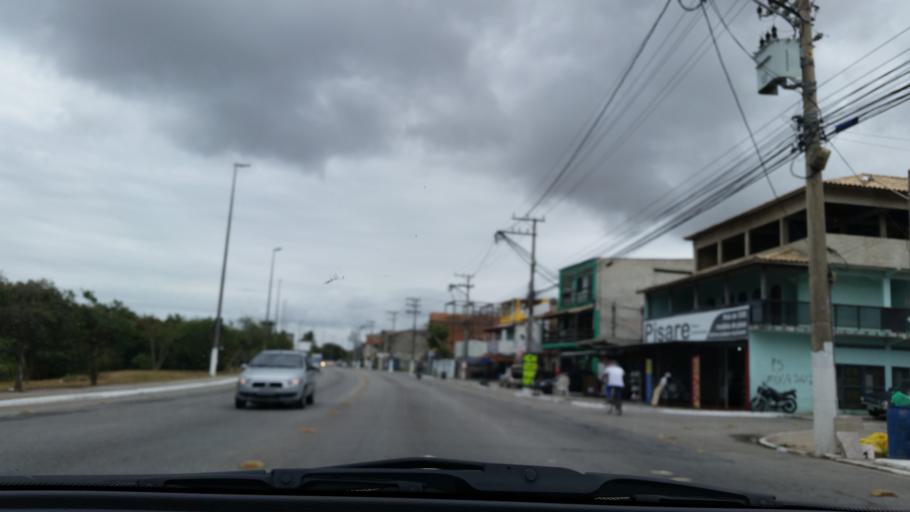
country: BR
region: Rio de Janeiro
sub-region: Cabo Frio
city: Cabo Frio
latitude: -22.8711
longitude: -42.0248
